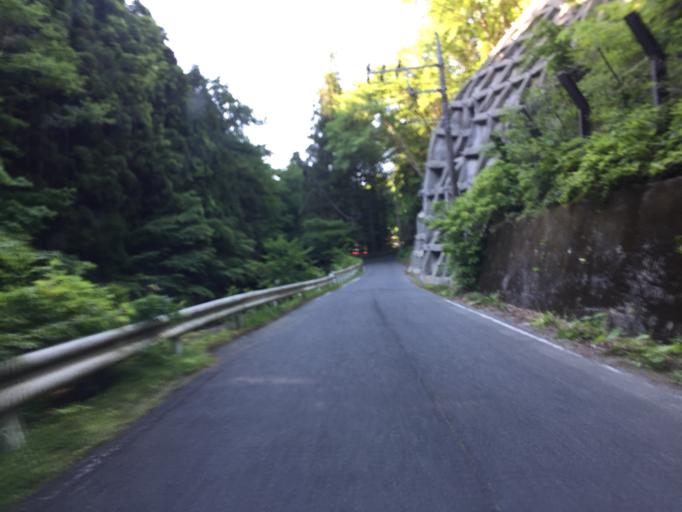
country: JP
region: Ibaraki
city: Kitaibaraki
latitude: 36.8612
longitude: 140.6376
